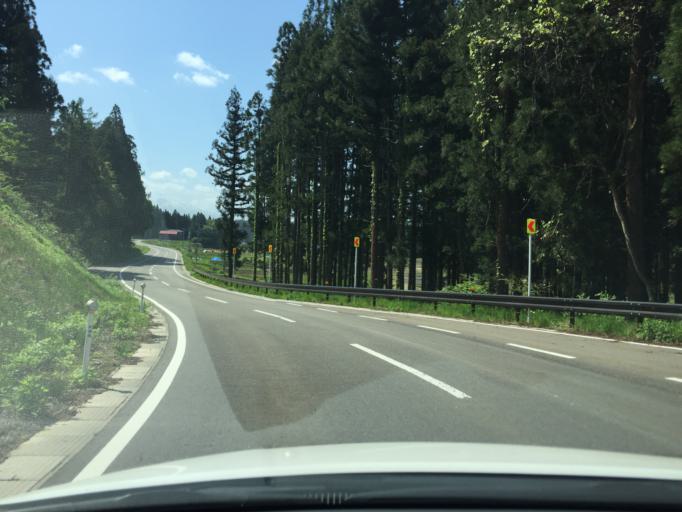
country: JP
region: Niigata
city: Kamo
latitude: 37.5715
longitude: 139.0835
